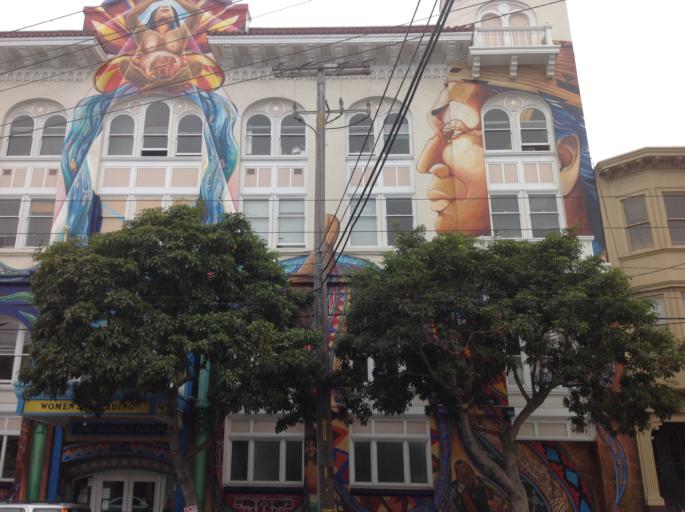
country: US
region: California
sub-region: San Francisco County
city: San Francisco
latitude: 37.7617
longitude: -122.4227
